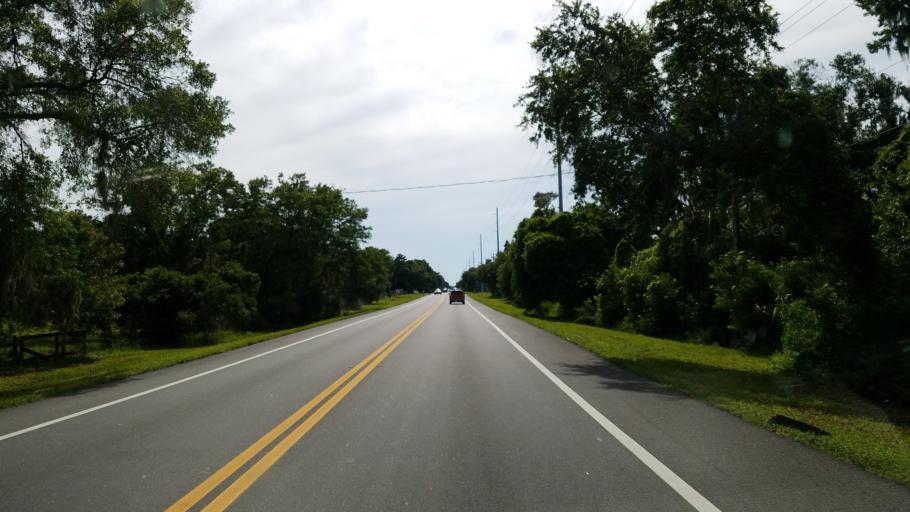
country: US
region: Florida
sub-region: Hillsborough County
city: Fish Hawk
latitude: 27.8502
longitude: -82.1550
